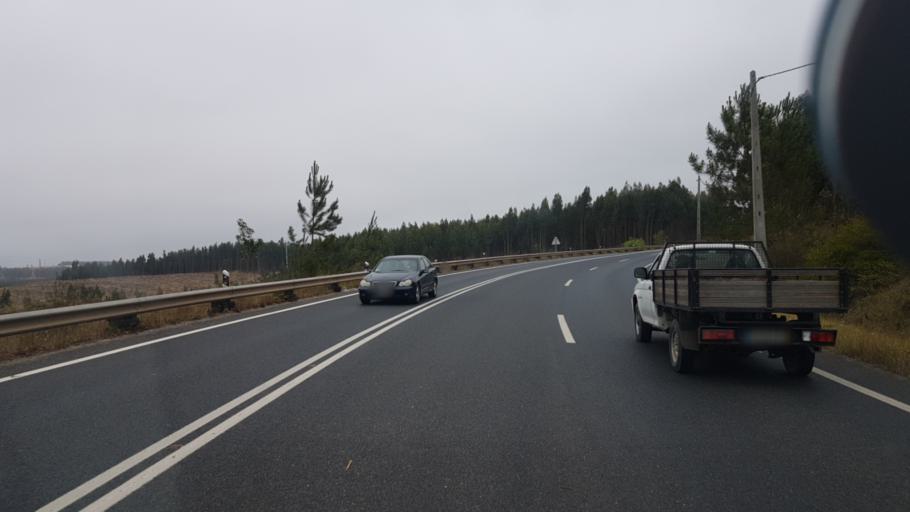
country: PT
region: Leiria
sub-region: Bombarral
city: Bombarral
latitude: 39.1766
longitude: -9.1978
